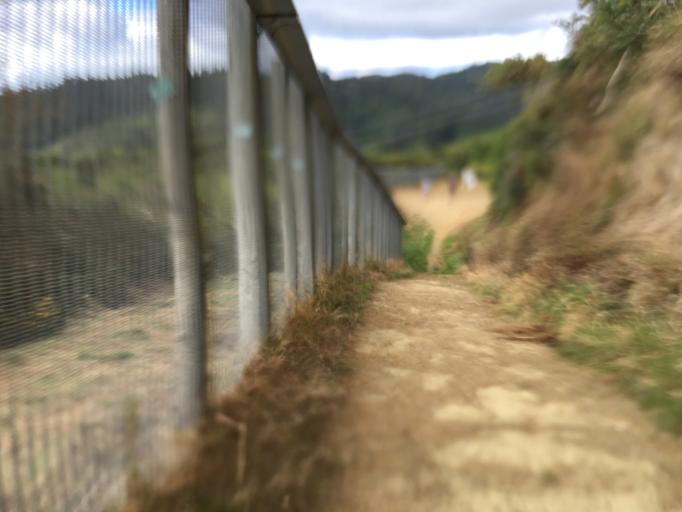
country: NZ
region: Wellington
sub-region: Wellington City
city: Brooklyn
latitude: -41.2993
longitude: 174.7384
